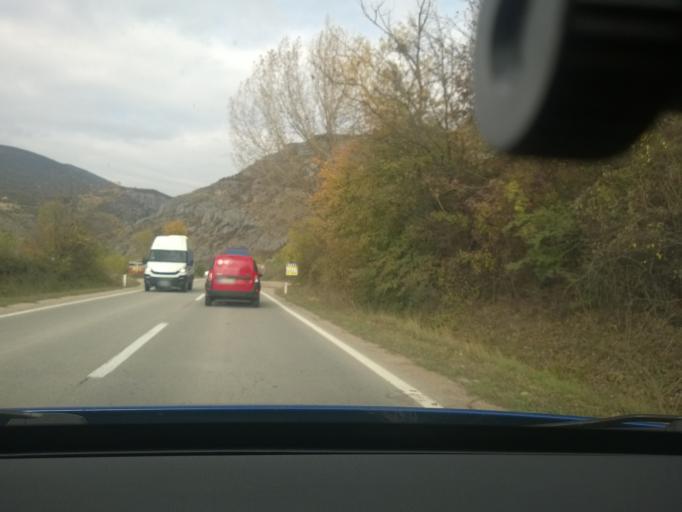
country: RS
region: Central Serbia
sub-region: Nisavski Okrug
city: Svrljig
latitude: 43.3065
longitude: 22.1893
